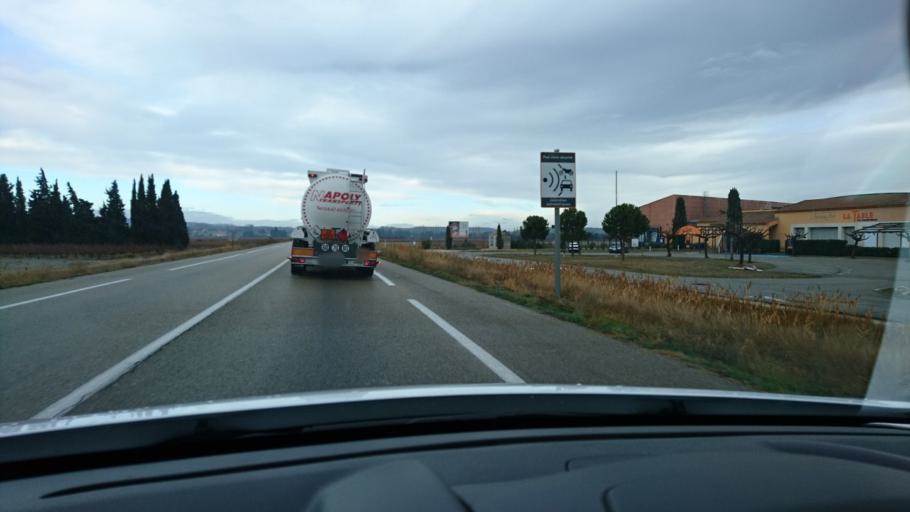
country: FR
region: Languedoc-Roussillon
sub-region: Departement du Gard
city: Pujaut
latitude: 43.9884
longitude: 4.7467
